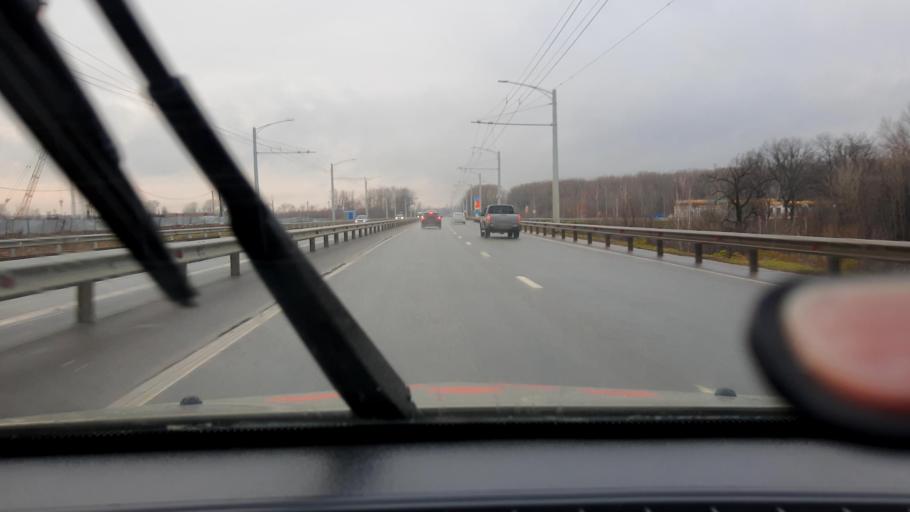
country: RU
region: Bashkortostan
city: Mikhaylovka
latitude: 54.7703
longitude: 55.9039
